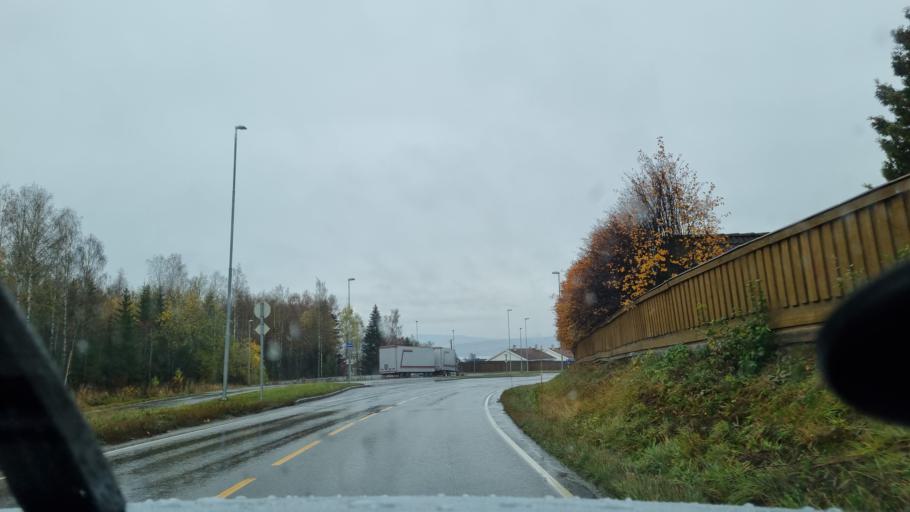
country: NO
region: Hedmark
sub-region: Hamar
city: Hamar
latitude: 60.8160
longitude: 11.0648
